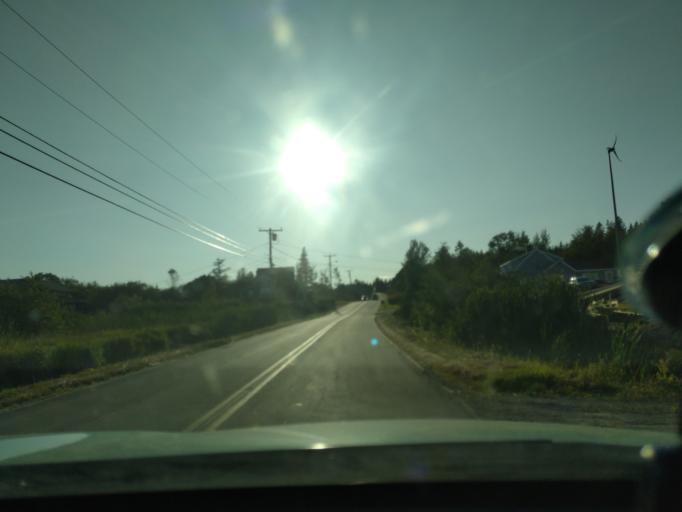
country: US
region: Maine
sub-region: Washington County
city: Machiasport
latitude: 44.6584
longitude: -67.2124
